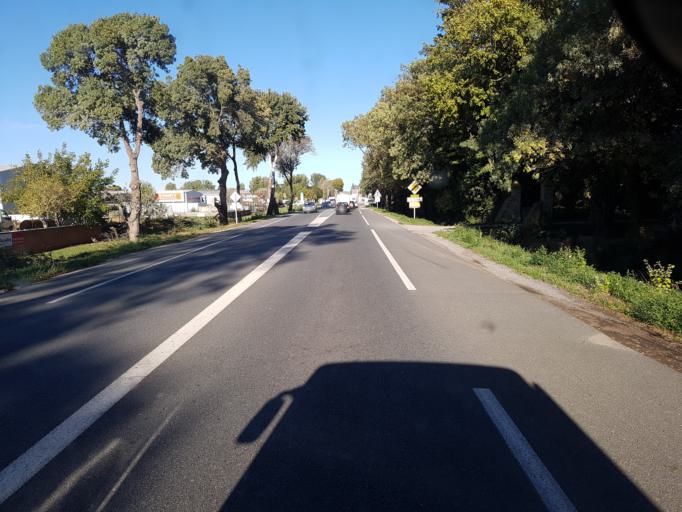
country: FR
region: Languedoc-Roussillon
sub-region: Departement de l'Aude
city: Coursan
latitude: 43.2268
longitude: 3.0485
